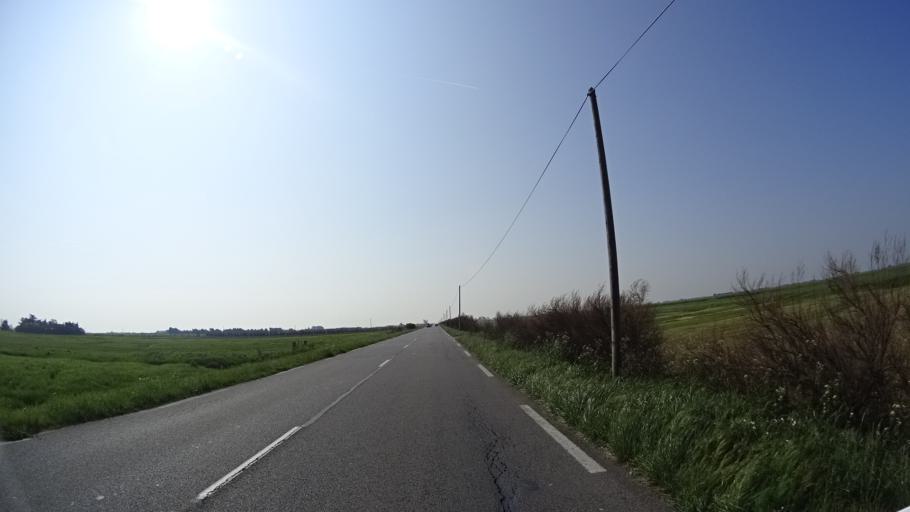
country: FR
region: Pays de la Loire
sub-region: Departement de la Loire-Atlantique
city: Bourgneuf-en-Retz
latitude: 47.0248
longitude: -1.9616
